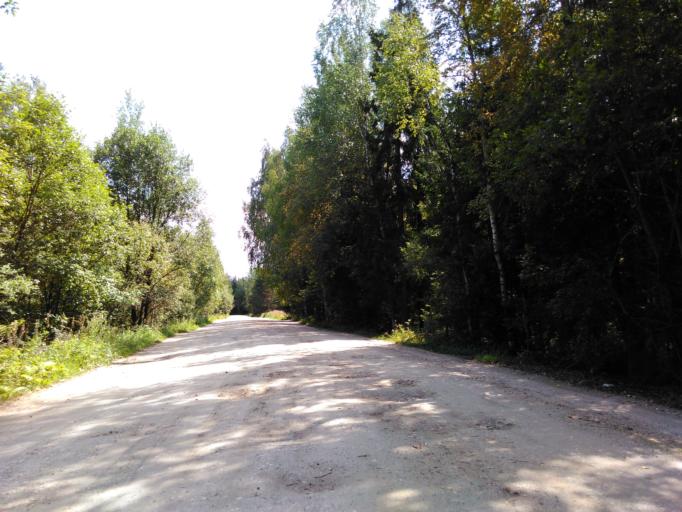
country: RU
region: Vladimir
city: Krasnyy Oktyabr'
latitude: 56.0130
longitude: 38.8123
